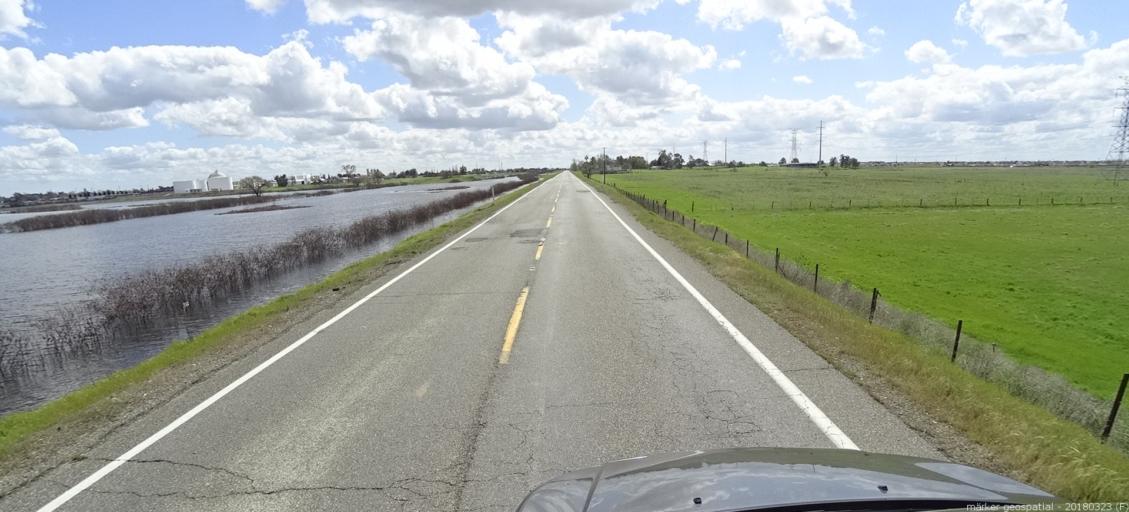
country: US
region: California
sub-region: Sacramento County
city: Elverta
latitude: 38.6936
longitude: -121.4856
